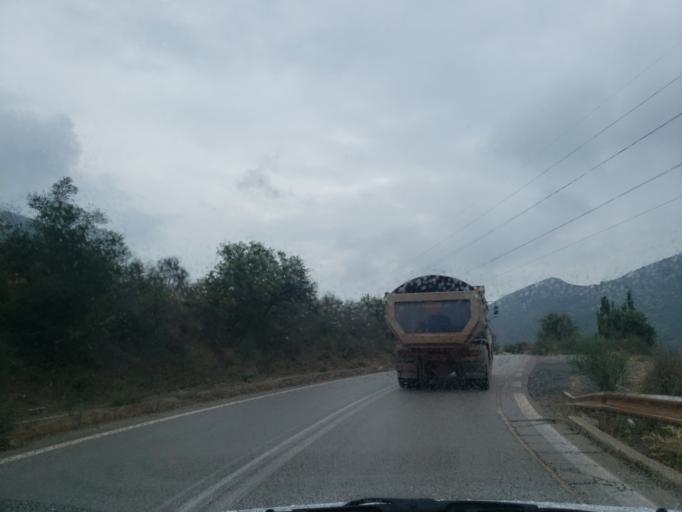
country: GR
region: Central Greece
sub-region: Nomos Fokidos
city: Amfissa
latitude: 38.5780
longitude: 22.3935
